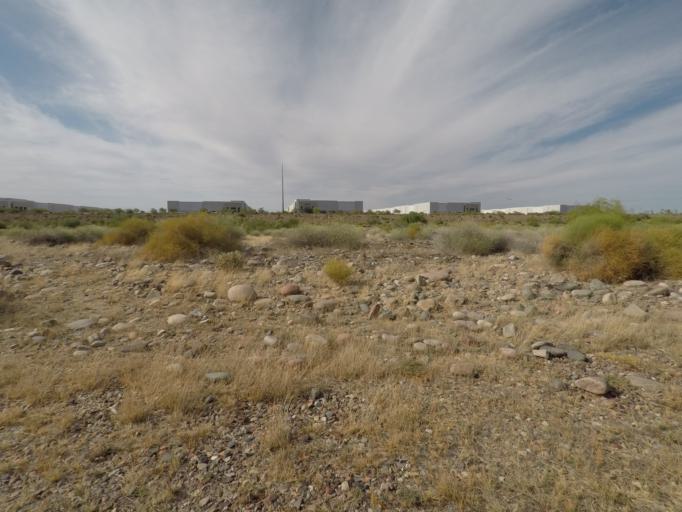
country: US
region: Arizona
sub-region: Maricopa County
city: Phoenix
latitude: 33.4158
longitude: -112.0343
